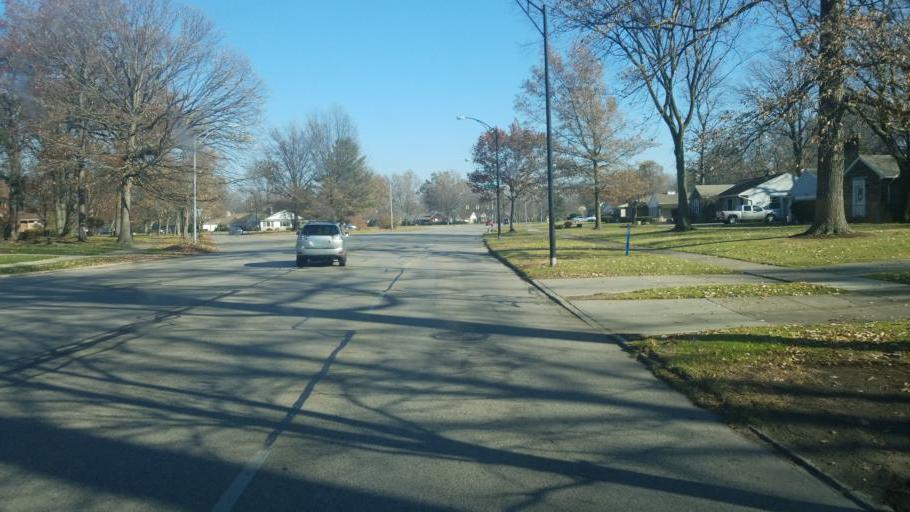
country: US
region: Ohio
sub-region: Cuyahoga County
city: Cleveland Heights
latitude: 41.5227
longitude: -81.5655
